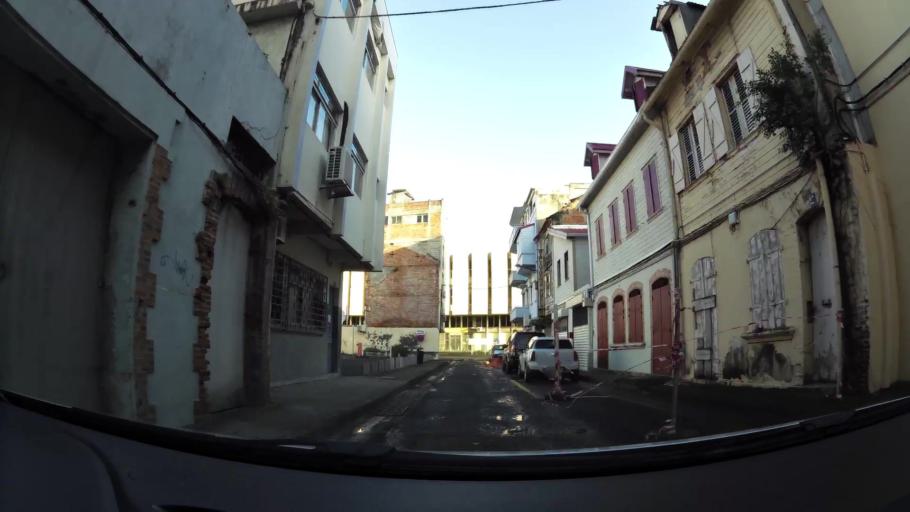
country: MQ
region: Martinique
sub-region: Martinique
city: Fort-de-France
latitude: 14.6044
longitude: -61.0659
